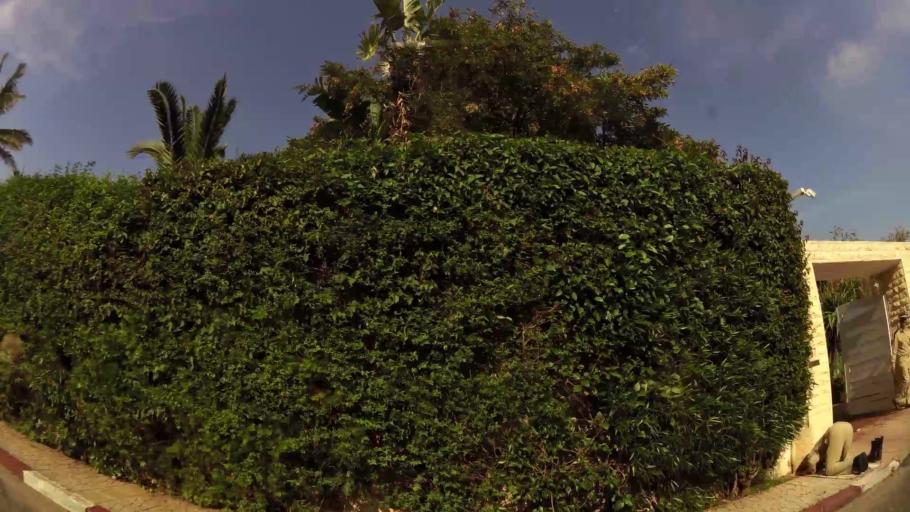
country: MA
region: Rabat-Sale-Zemmour-Zaer
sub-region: Rabat
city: Rabat
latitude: 33.9347
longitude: -6.8049
